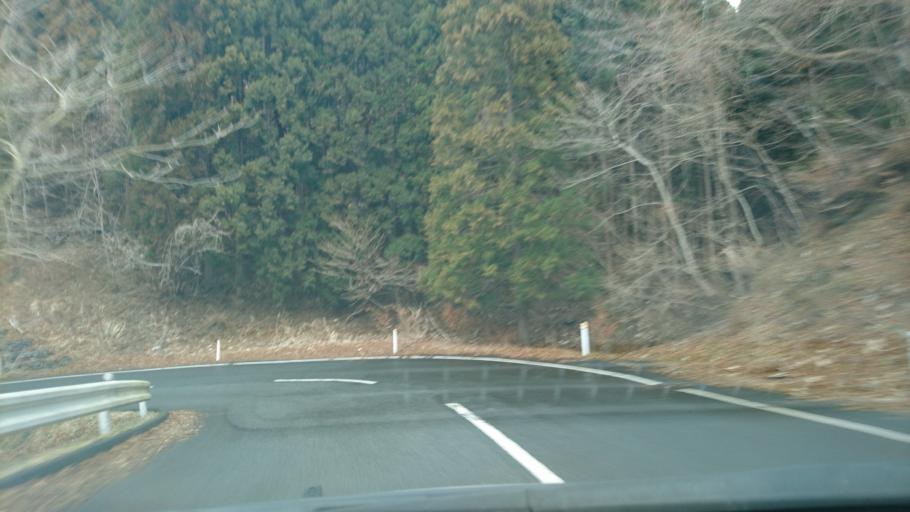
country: JP
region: Iwate
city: Ofunato
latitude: 38.9980
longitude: 141.5490
